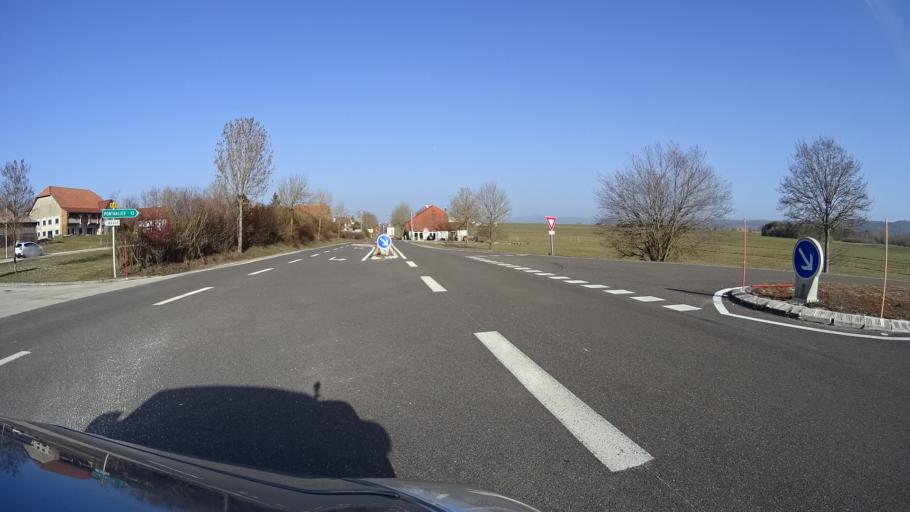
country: FR
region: Franche-Comte
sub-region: Departement du Doubs
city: Frasne
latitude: 46.8900
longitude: 6.2202
